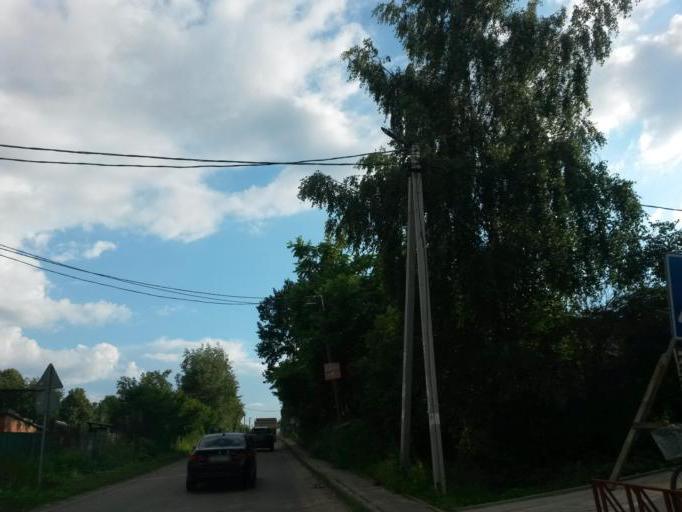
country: RU
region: Moskovskaya
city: Barybino
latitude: 55.2523
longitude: 37.8206
